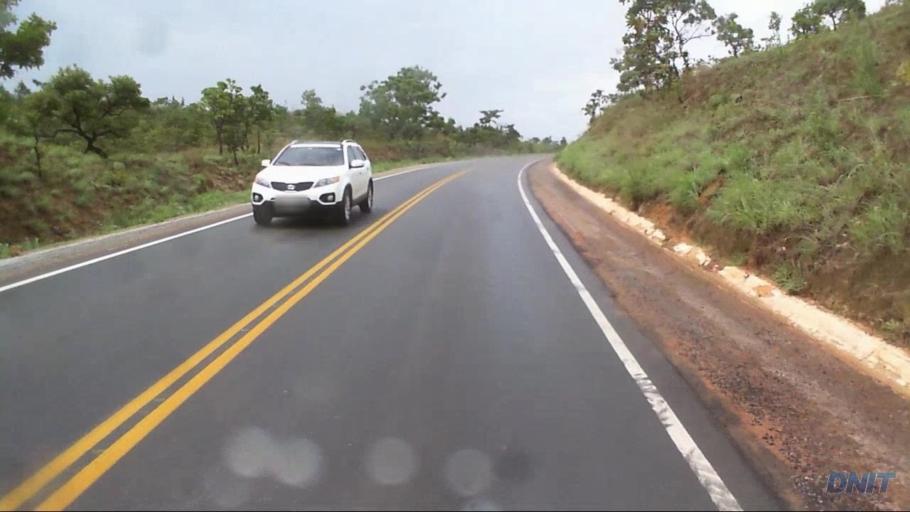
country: BR
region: Goias
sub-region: Padre Bernardo
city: Padre Bernardo
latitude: -15.4616
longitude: -48.2176
